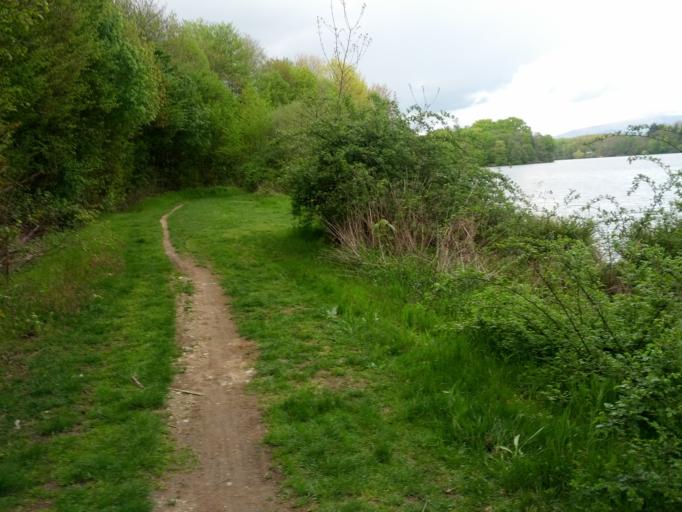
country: DE
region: Baden-Wuerttemberg
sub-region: Freiburg Region
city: Umkirch
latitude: 48.0070
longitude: 7.7542
